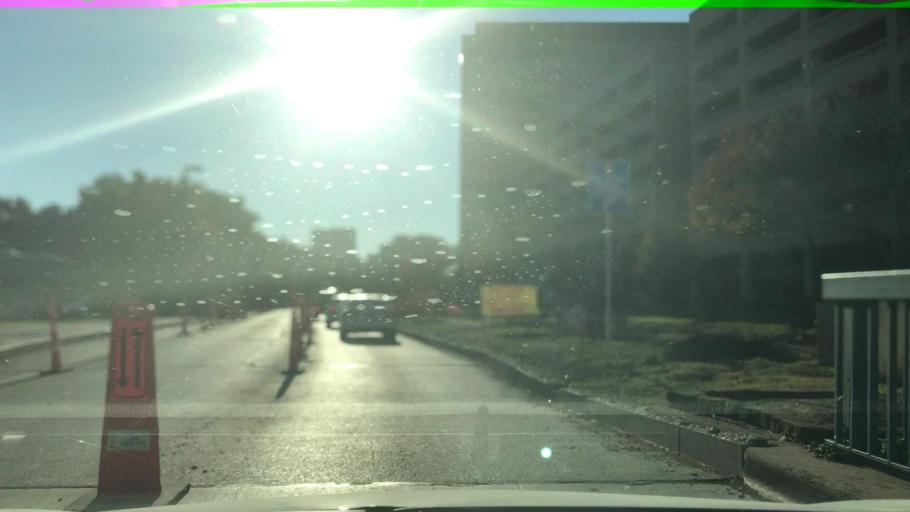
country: US
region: Texas
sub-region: Dallas County
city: Irving
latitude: 32.8677
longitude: -96.9400
